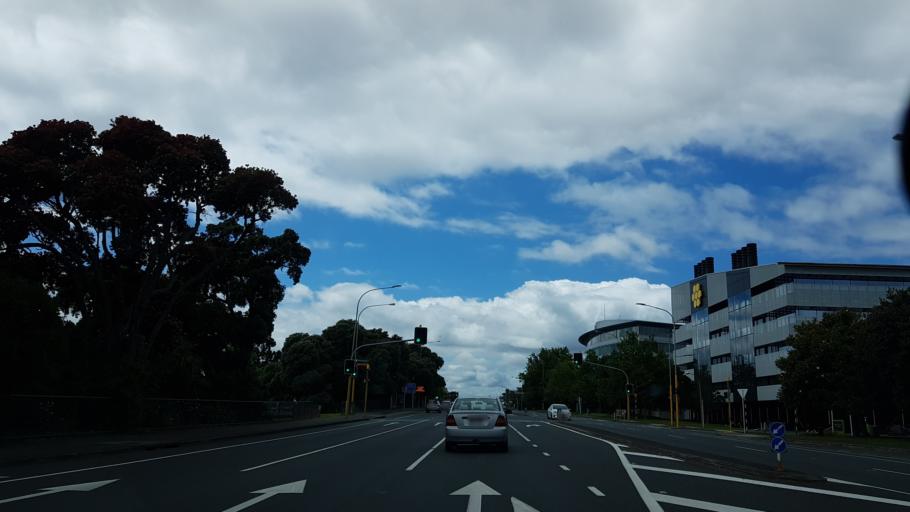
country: NZ
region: Auckland
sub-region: Auckland
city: North Shore
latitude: -36.7835
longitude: 174.7540
